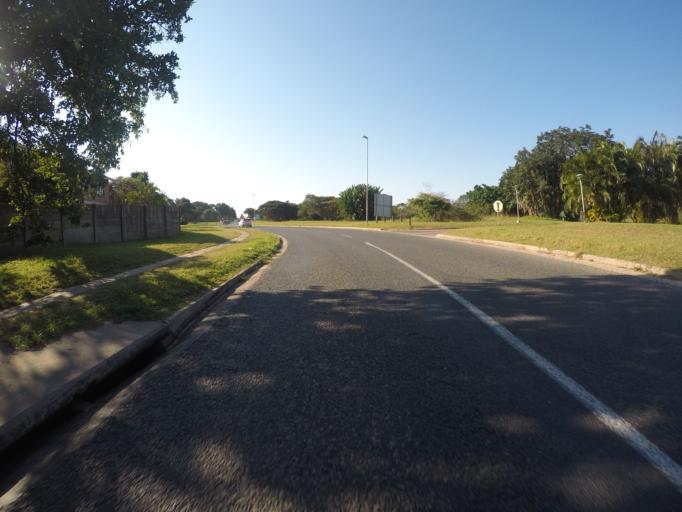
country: ZA
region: KwaZulu-Natal
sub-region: uThungulu District Municipality
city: Richards Bay
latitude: -28.7918
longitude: 32.0981
